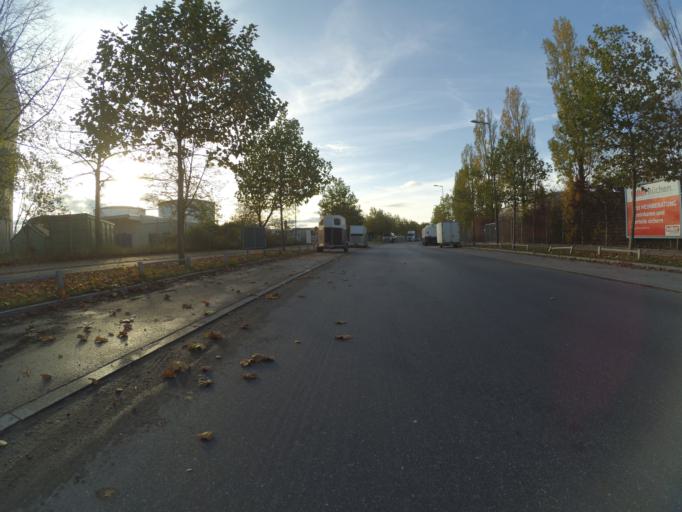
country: DE
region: Bavaria
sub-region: Upper Bavaria
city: Munich
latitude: 48.1926
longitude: 11.5611
